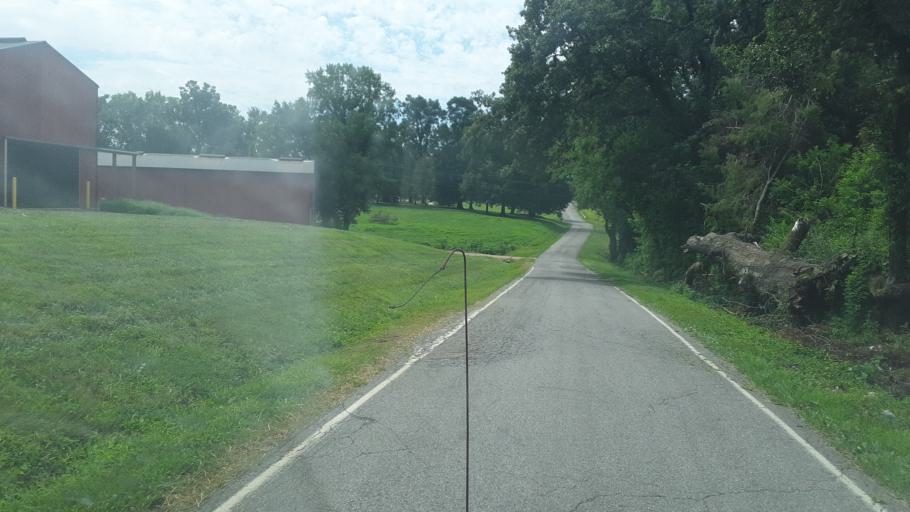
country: US
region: Kentucky
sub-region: Christian County
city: Oak Grove
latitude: 36.6498
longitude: -87.3440
